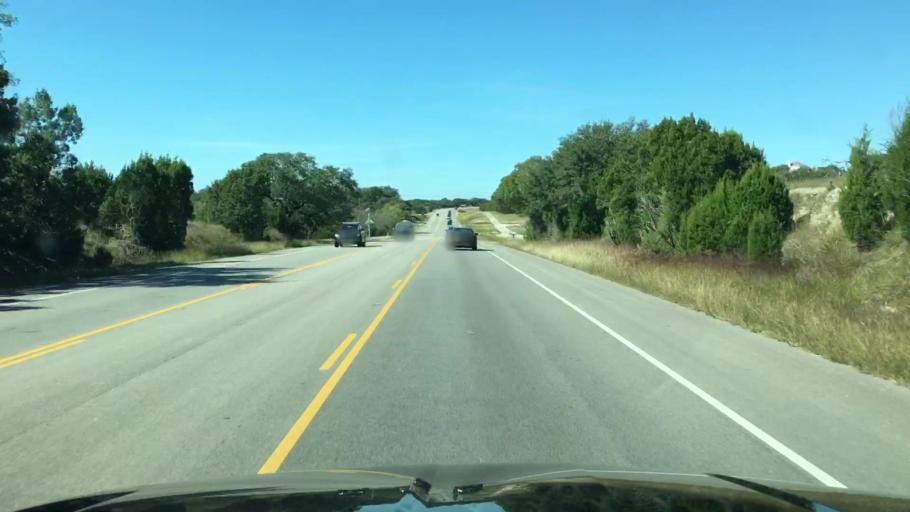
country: US
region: Texas
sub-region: Hays County
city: Dripping Springs
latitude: 30.1976
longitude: -98.1674
